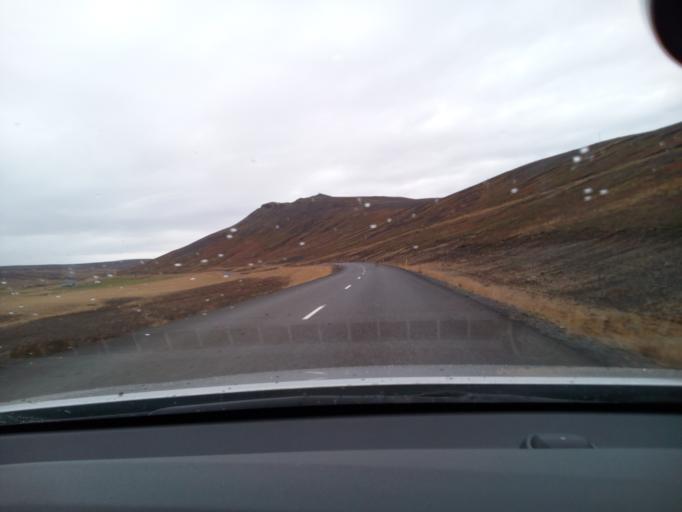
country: IS
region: Northeast
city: Laugar
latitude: 65.8062
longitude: -17.2654
